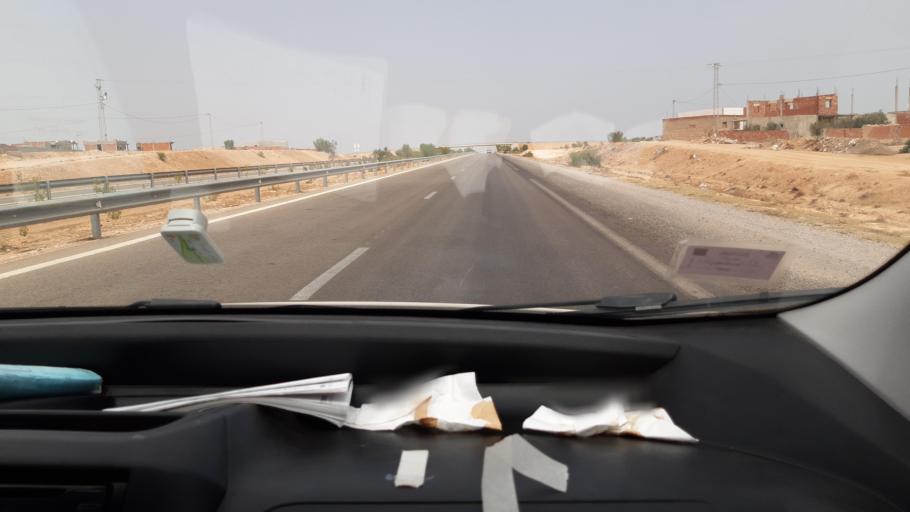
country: TN
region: Safaqis
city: Sfax
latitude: 34.8415
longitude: 10.6680
